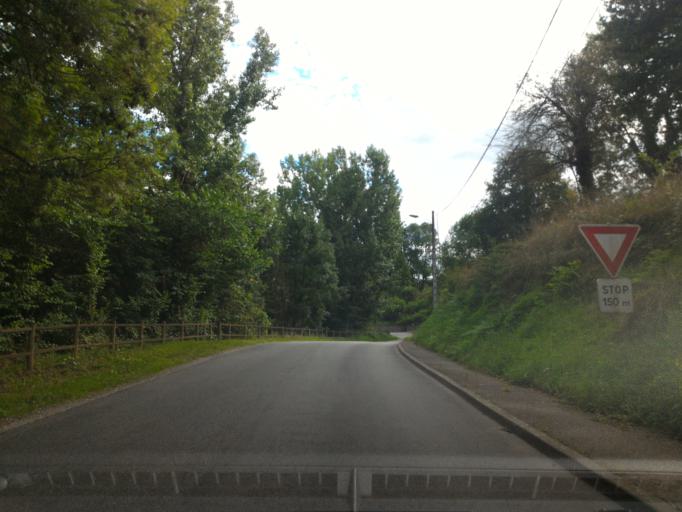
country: FR
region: Limousin
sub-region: Departement de la Haute-Vienne
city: Saint-Junien
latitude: 45.8900
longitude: 0.8859
